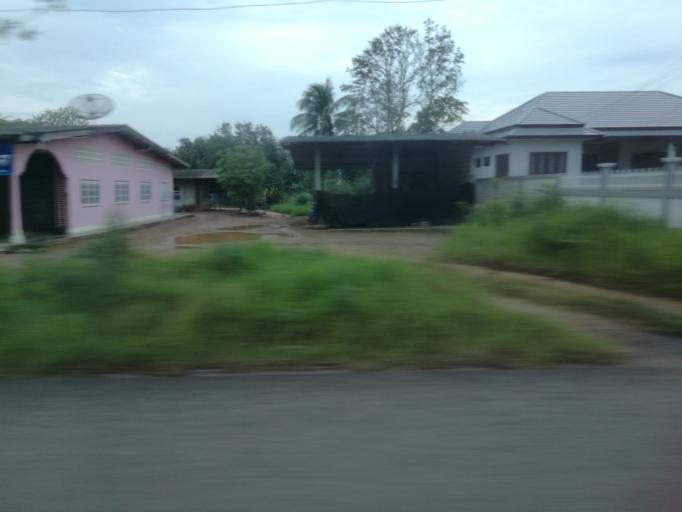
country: TH
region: Prachuap Khiri Khan
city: Prachuap Khiri Khan
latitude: 11.8699
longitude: 99.7860
